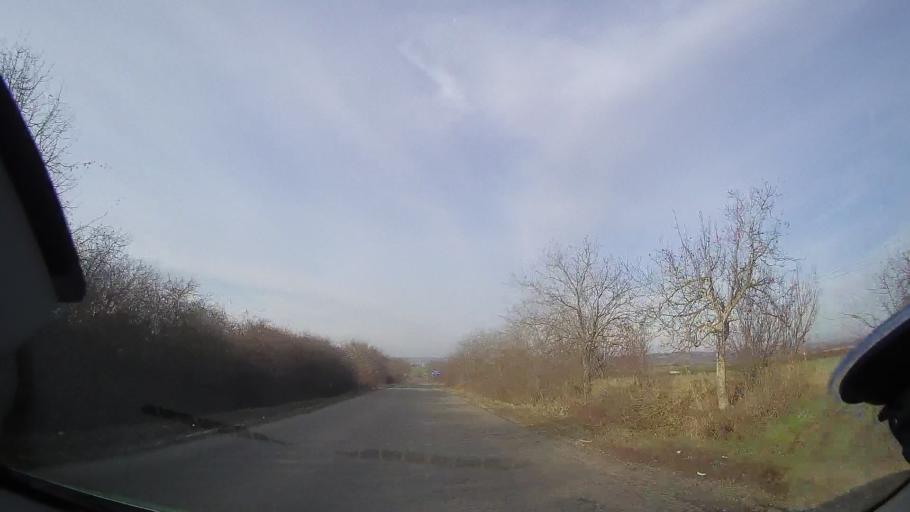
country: RO
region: Bihor
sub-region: Comuna Spinus
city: Spinus
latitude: 47.2248
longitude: 22.1686
